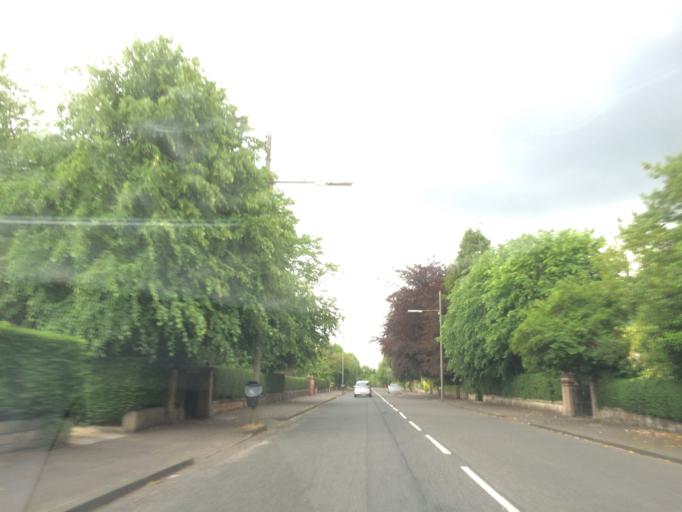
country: GB
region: Scotland
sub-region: East Renfrewshire
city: Giffnock
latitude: 55.8175
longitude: -4.2781
